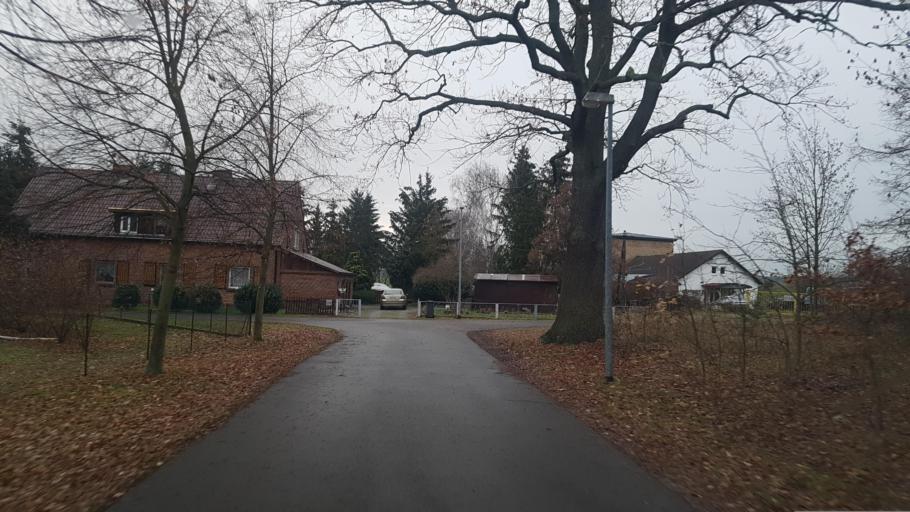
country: DE
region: Brandenburg
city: Drebkau
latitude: 51.6629
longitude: 14.2538
